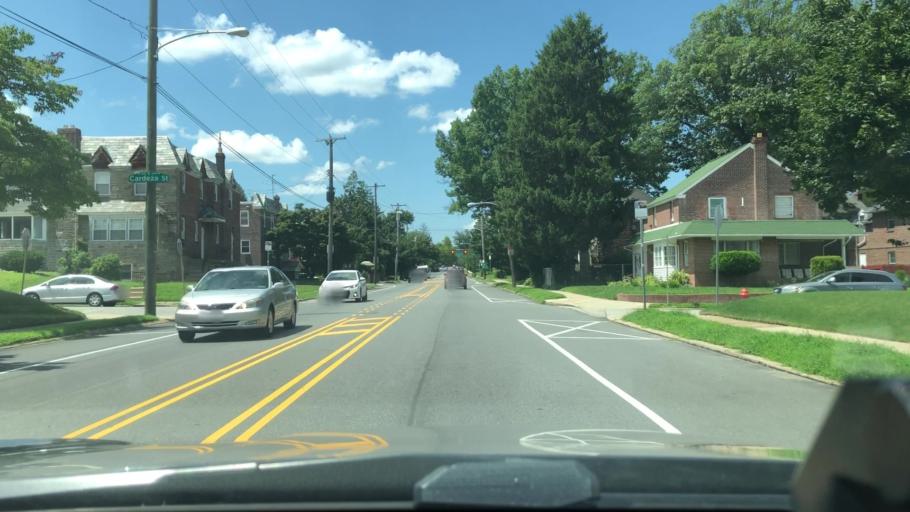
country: US
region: Pennsylvania
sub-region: Montgomery County
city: Wyndmoor
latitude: 40.0616
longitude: -75.1690
